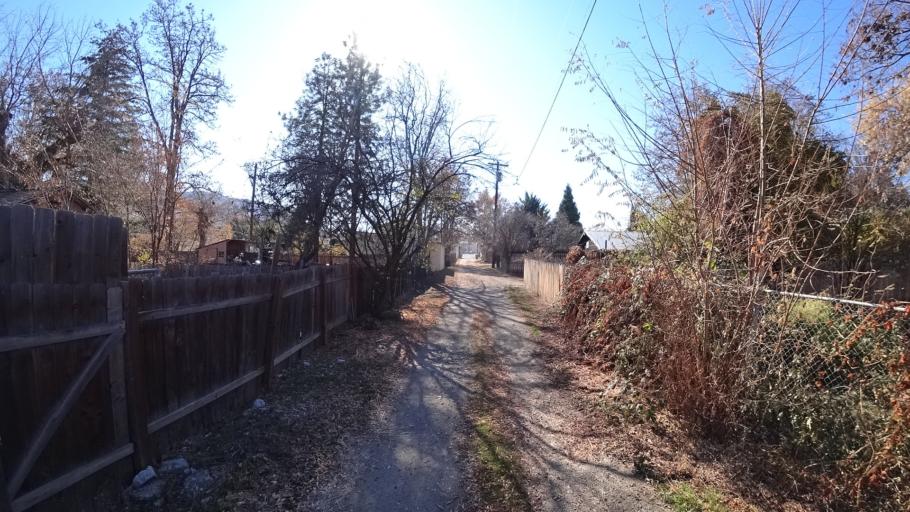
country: US
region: California
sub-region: Siskiyou County
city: Yreka
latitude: 41.7348
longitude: -122.6366
